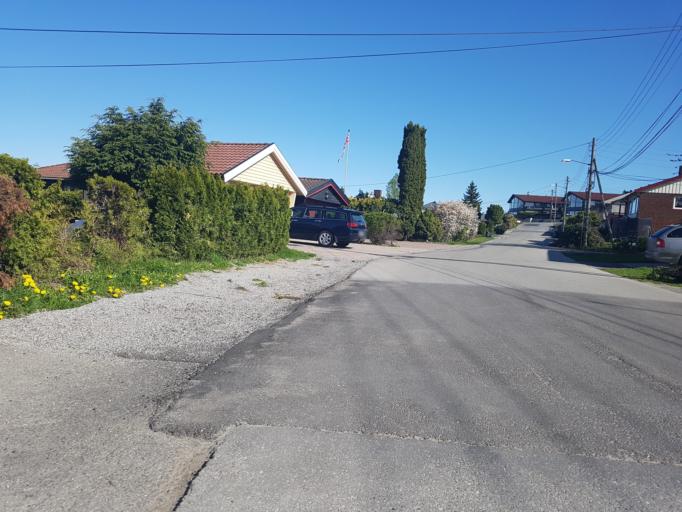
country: NO
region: Buskerud
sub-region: Drammen
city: Drammen
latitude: 59.7225
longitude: 10.2110
